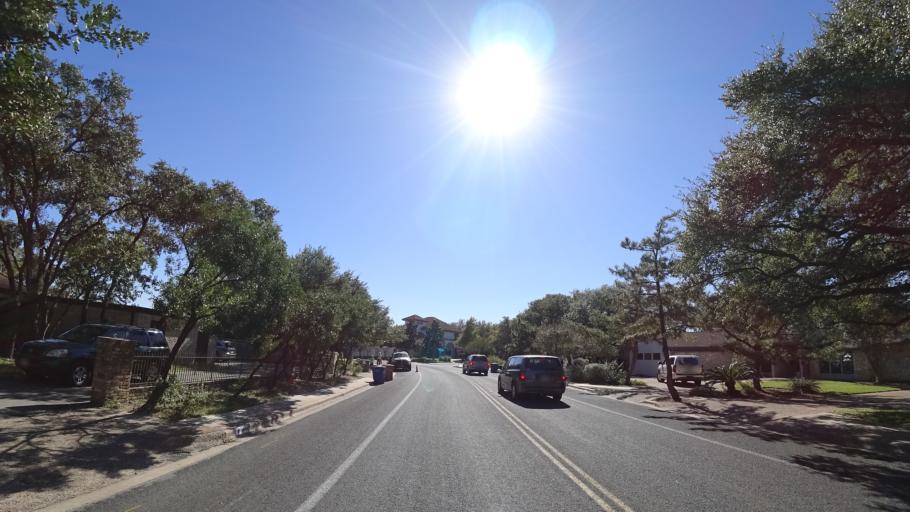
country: US
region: Texas
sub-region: Travis County
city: West Lake Hills
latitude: 30.3521
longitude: -97.7718
